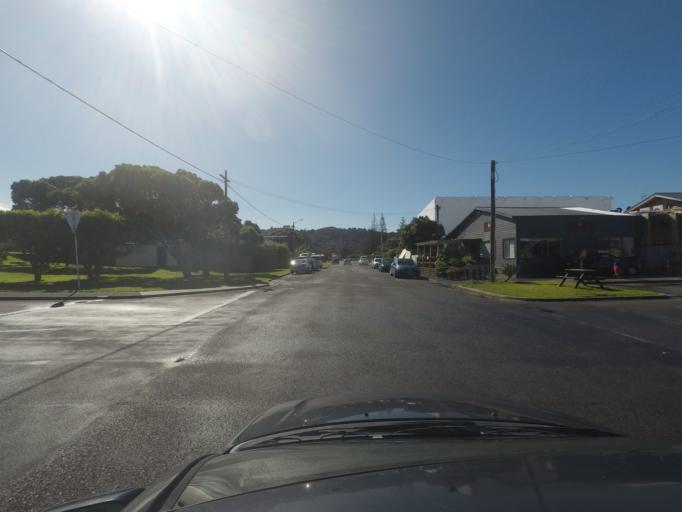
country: NZ
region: Bay of Plenty
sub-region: Western Bay of Plenty District
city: Waihi Beach
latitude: -37.4059
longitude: 175.9430
